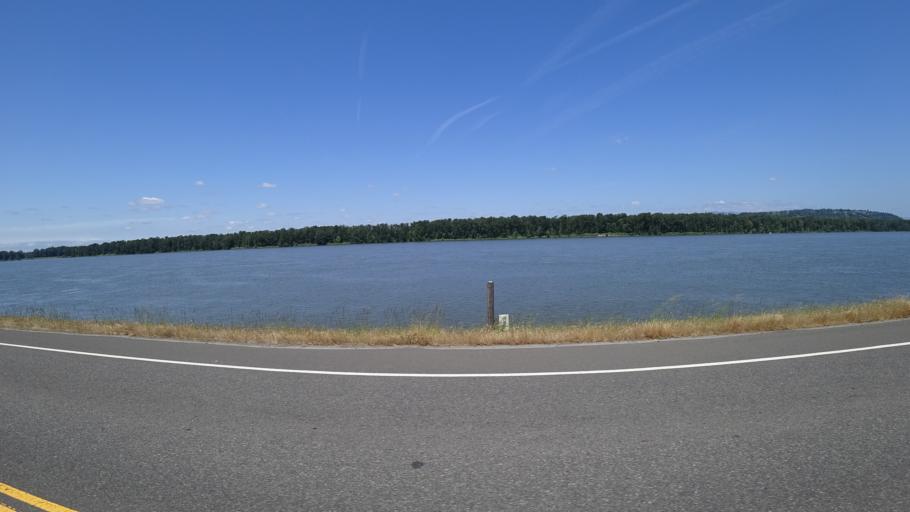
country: US
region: Oregon
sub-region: Multnomah County
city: Fairview
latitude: 45.5605
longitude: -122.4943
